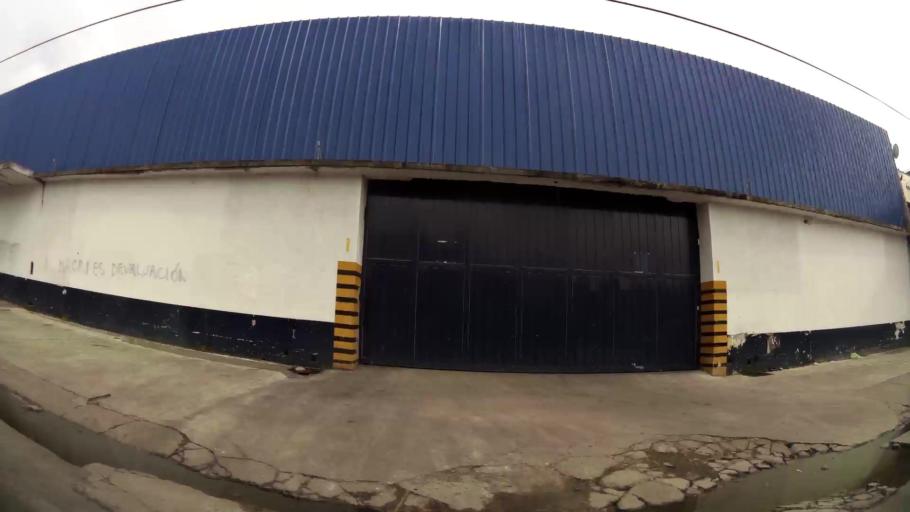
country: AR
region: Buenos Aires
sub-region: Partido de Quilmes
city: Quilmes
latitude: -34.7385
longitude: -58.2728
